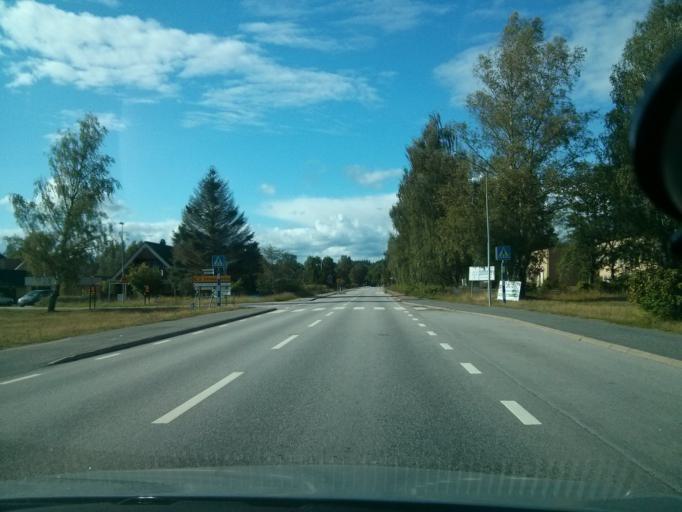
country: SE
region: Blekinge
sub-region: Ronneby Kommun
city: Brakne-Hoby
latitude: 56.3421
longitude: 15.1576
